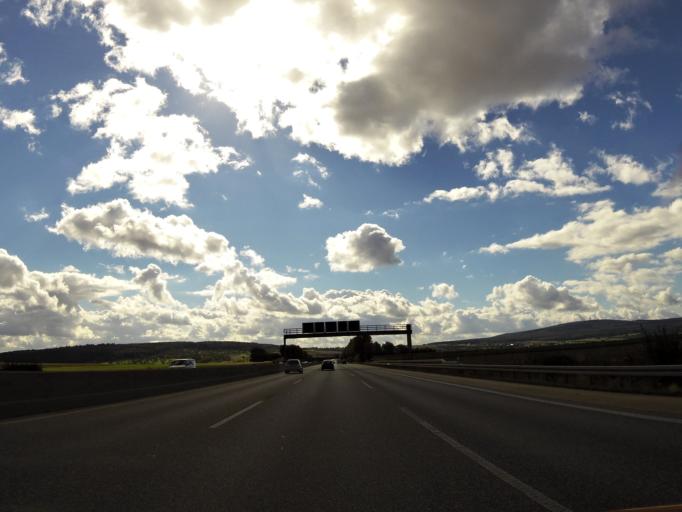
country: DE
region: Hesse
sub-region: Regierungsbezirk Darmstadt
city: Ober-Morlen
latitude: 50.3928
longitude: 8.7029
